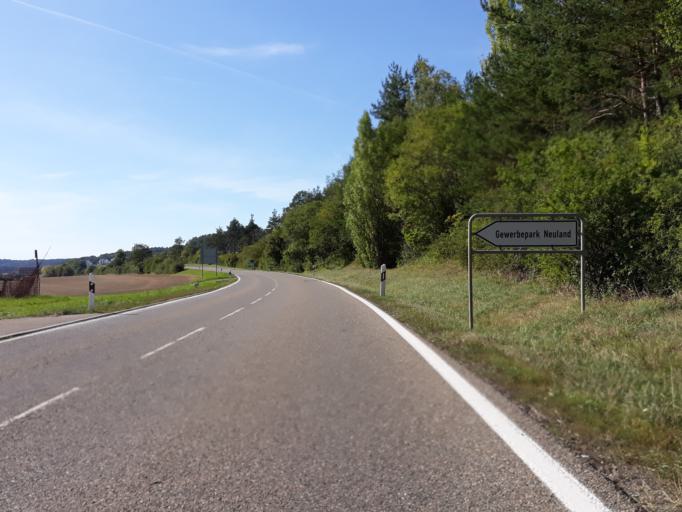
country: DE
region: Baden-Wuerttemberg
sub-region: Regierungsbezirk Stuttgart
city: Weil der Stadt
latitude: 48.7253
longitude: 8.8743
